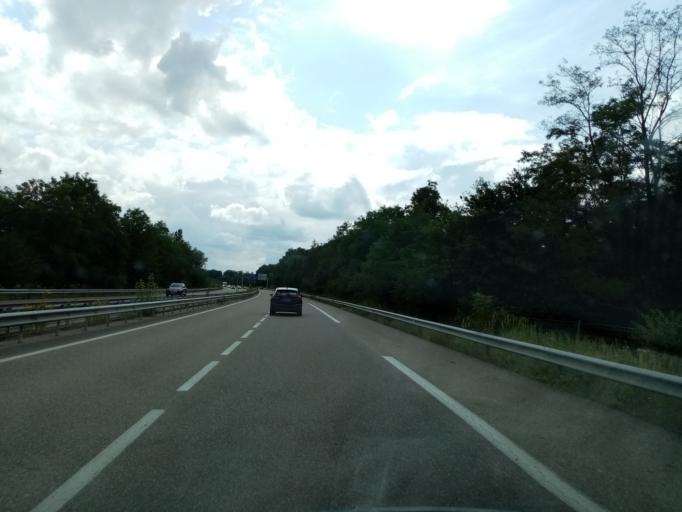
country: FR
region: Alsace
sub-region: Departement du Bas-Rhin
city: Seltz
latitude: 48.9003
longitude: 8.0903
